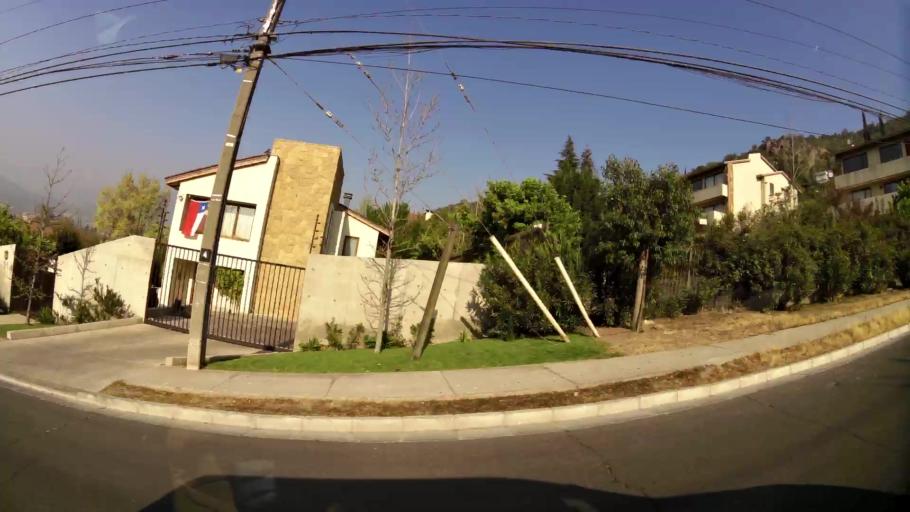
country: CL
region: Santiago Metropolitan
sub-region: Provincia de Santiago
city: Villa Presidente Frei, Nunoa, Santiago, Chile
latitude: -33.3672
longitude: -70.5296
